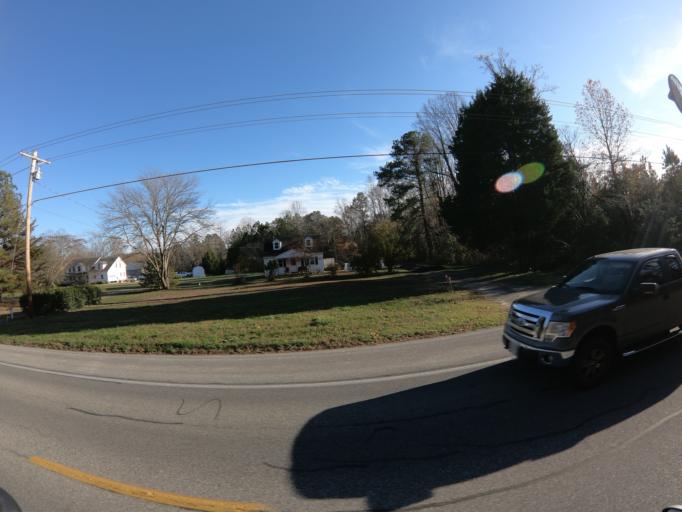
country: US
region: Maryland
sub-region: Saint Mary's County
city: Mechanicsville
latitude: 38.3948
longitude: -76.6598
